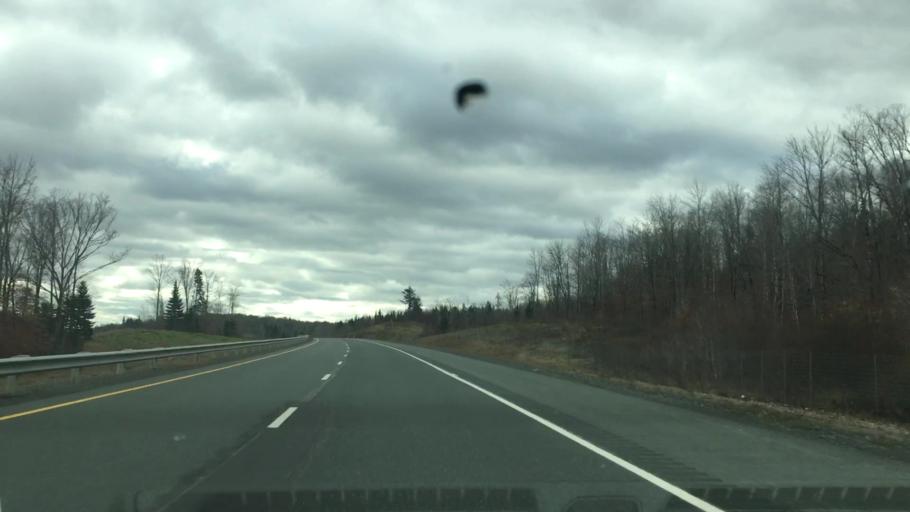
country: US
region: Maine
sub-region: Aroostook County
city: Fort Fairfield
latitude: 46.6448
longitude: -67.7437
